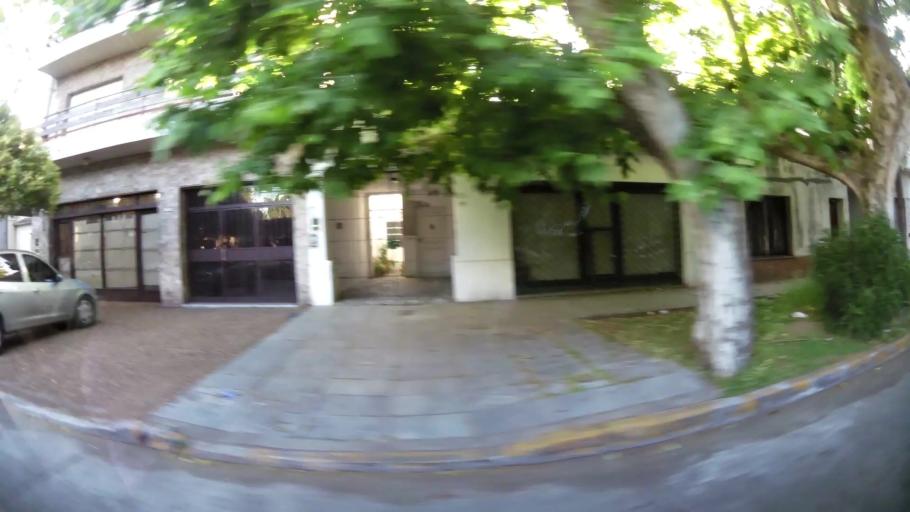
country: AR
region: Buenos Aires
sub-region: Partido de General San Martin
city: General San Martin
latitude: -34.5664
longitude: -58.5402
